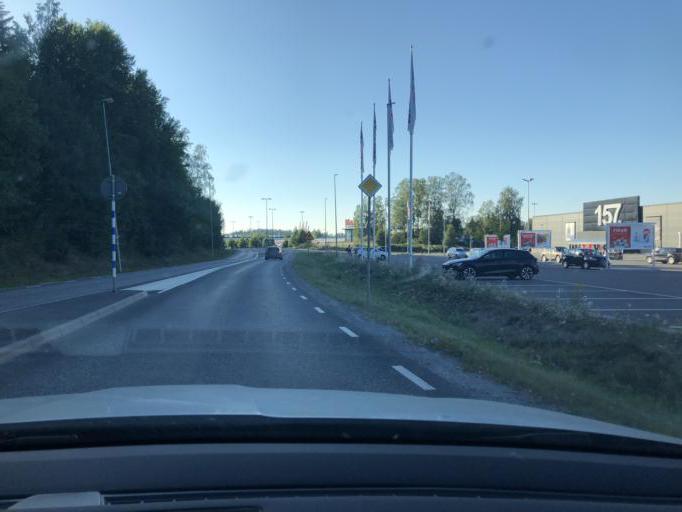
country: SE
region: Stockholm
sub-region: Sodertalje Kommun
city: Soedertaelje
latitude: 59.1853
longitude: 17.5832
